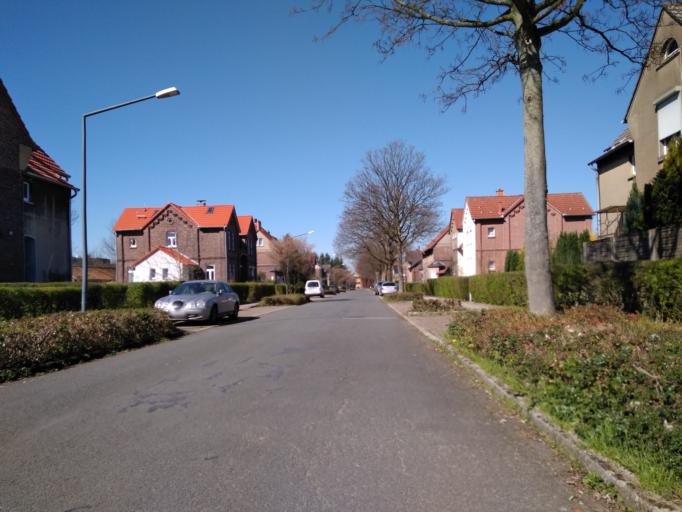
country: DE
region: North Rhine-Westphalia
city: Herten
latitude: 51.6139
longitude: 7.1128
